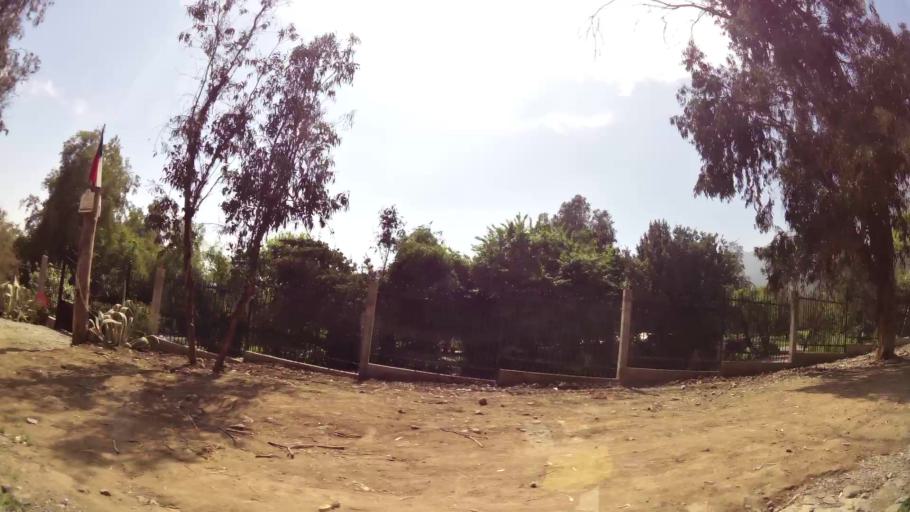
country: CL
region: Santiago Metropolitan
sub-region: Provincia de Santiago
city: Villa Presidente Frei, Nunoa, Santiago, Chile
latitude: -33.4671
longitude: -70.5255
